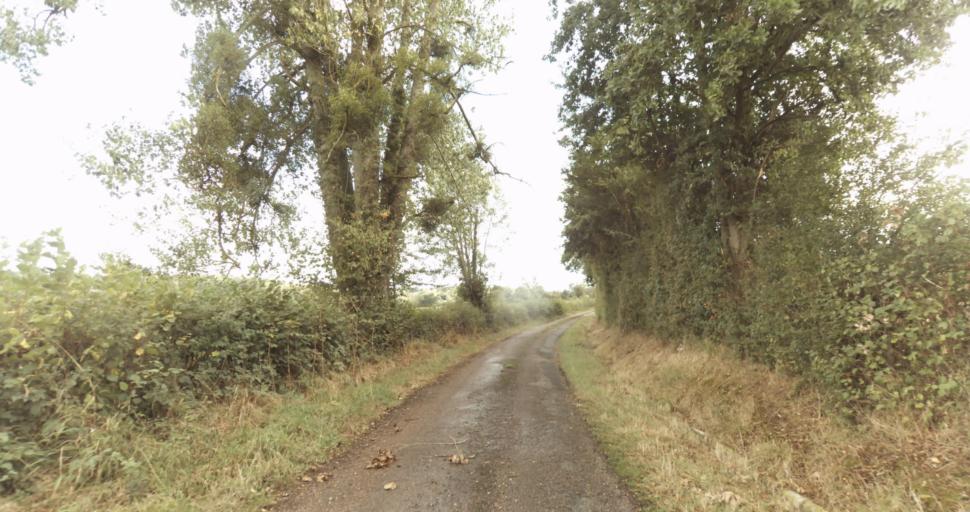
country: FR
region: Lower Normandy
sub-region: Departement de l'Orne
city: Vimoutiers
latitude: 48.8861
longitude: 0.1759
